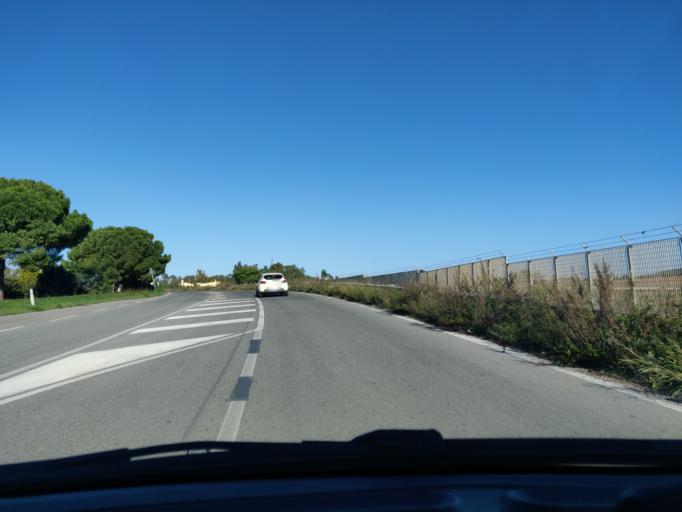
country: IT
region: Latium
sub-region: Citta metropolitana di Roma Capitale
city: Aurelia
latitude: 42.1271
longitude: 11.7725
